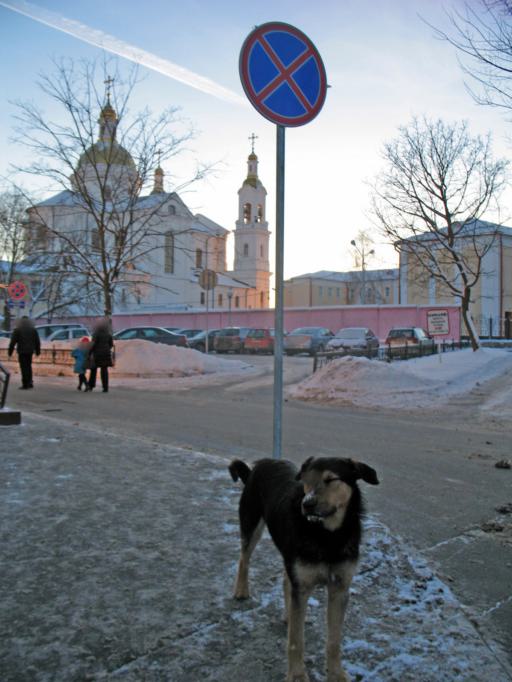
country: BY
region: Vitebsk
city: Vitebsk
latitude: 55.1973
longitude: 30.2038
